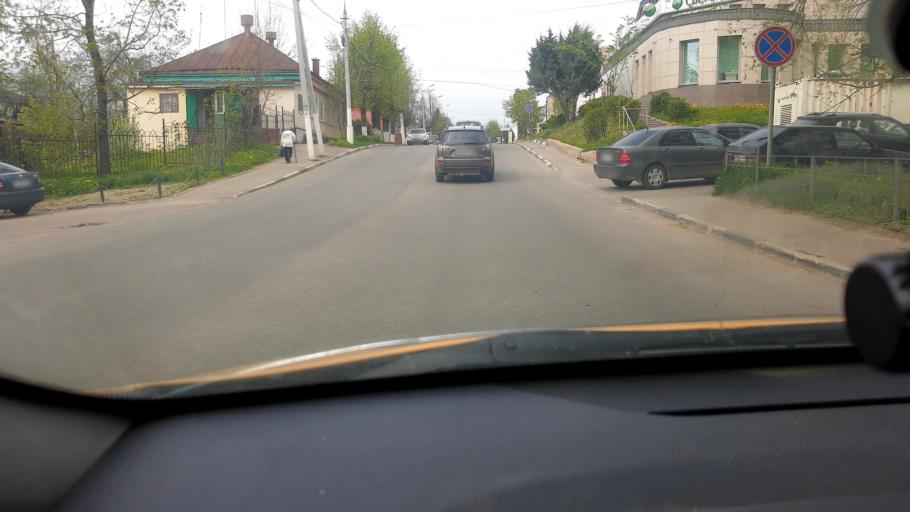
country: RU
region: Moskovskaya
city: Ruza
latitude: 55.7020
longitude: 36.1959
